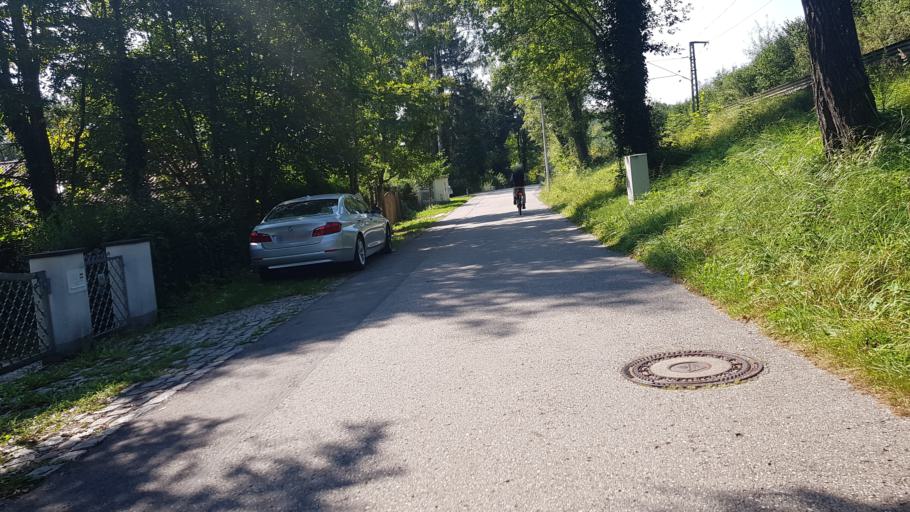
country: DE
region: Bavaria
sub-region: Upper Bavaria
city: Herrsching am Ammersee
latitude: 48.0259
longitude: 11.1809
